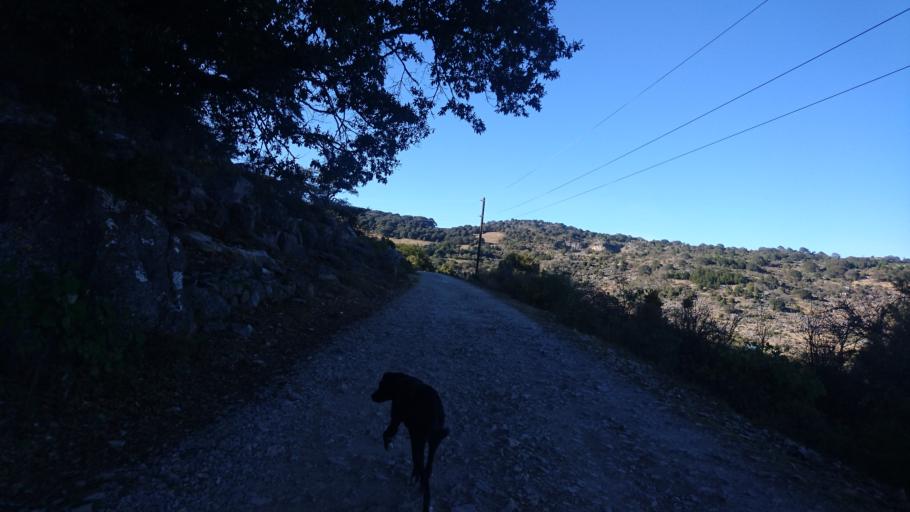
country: MX
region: San Luis Potosi
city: Zaragoza
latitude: 22.0303
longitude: -100.6044
